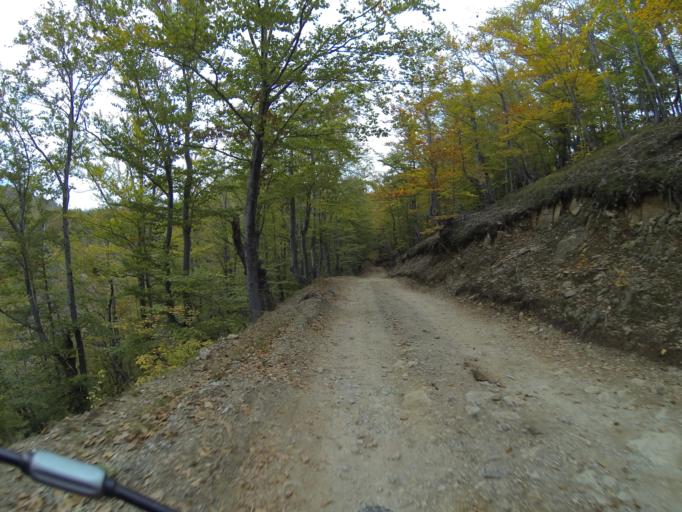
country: RO
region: Gorj
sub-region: Comuna Tismana
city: Sohodol
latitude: 45.0722
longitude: 22.8625
